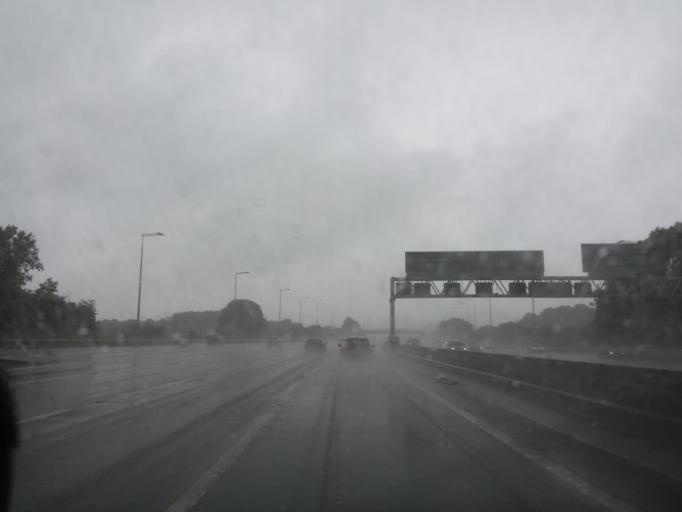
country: GB
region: England
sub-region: Nottinghamshire
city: Kimberley
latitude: 52.9858
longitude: -1.2394
